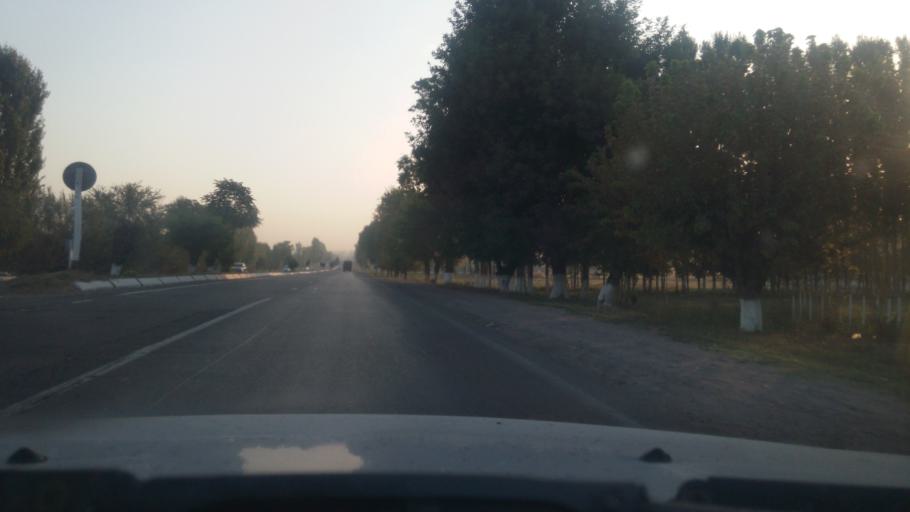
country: UZ
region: Toshkent
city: Urtaowul
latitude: 41.1787
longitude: 69.0767
